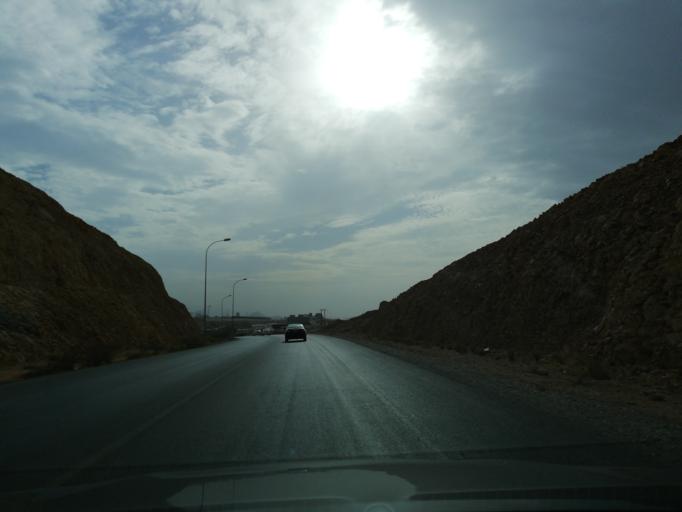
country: OM
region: Muhafazat Masqat
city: Bawshar
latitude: 23.4781
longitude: 58.3013
